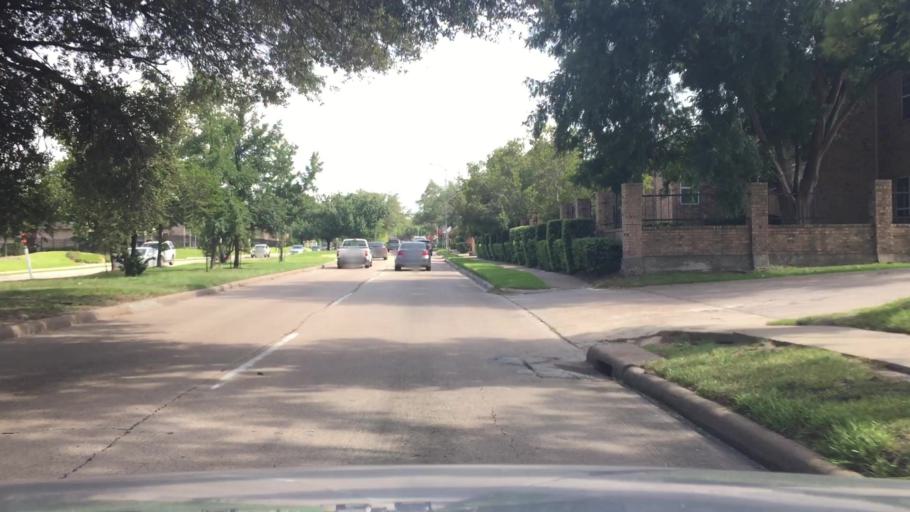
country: US
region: Texas
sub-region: Harris County
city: Bunker Hill Village
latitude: 29.7599
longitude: -95.5765
